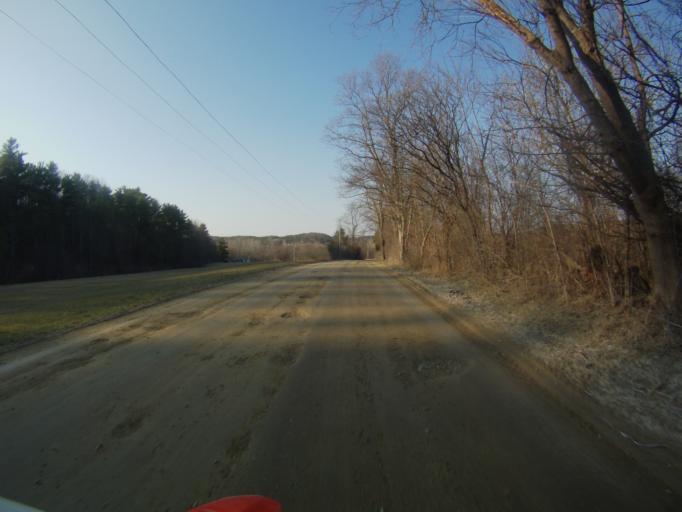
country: US
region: Vermont
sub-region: Addison County
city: Middlebury (village)
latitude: 44.0557
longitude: -73.1463
